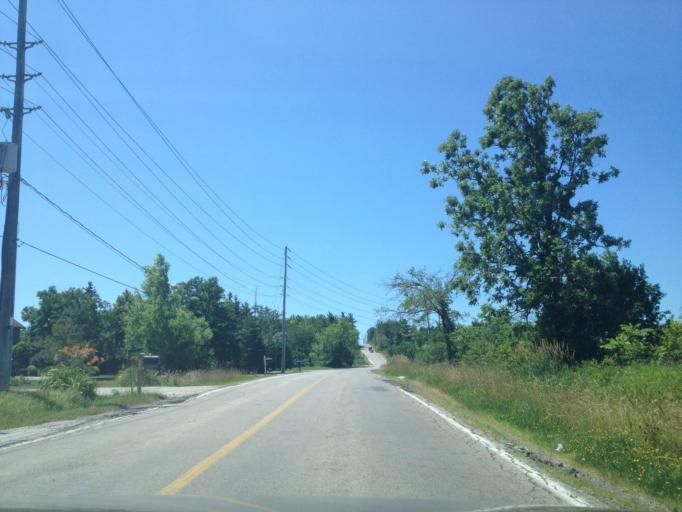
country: CA
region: Ontario
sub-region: Halton
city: Milton
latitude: 43.6621
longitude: -79.9521
